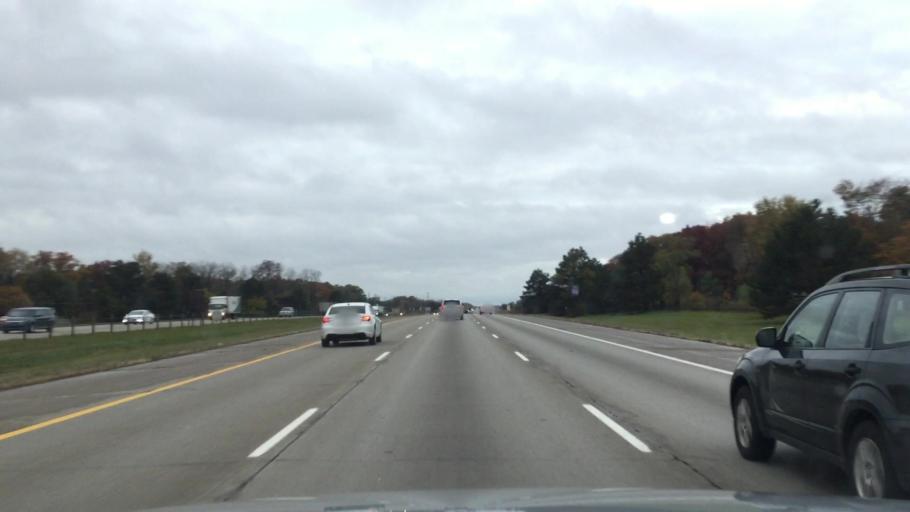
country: US
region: Michigan
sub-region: Wayne County
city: Belleville
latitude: 42.2197
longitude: -83.4952
